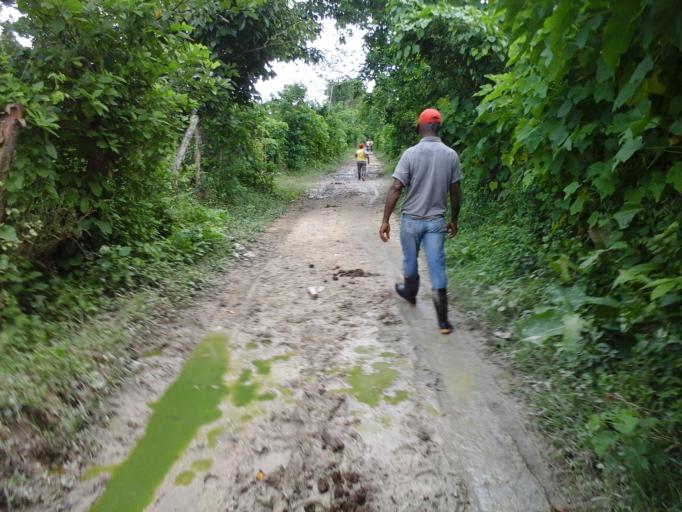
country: CO
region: Bolivar
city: San Pablo
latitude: 10.1538
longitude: -75.2734
